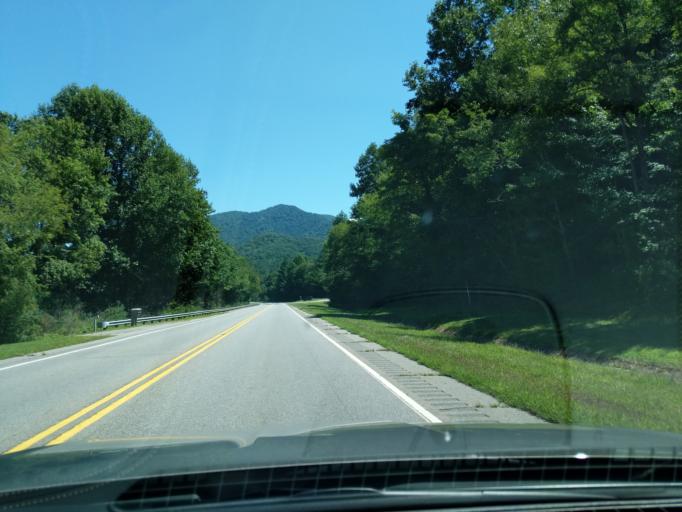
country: US
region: North Carolina
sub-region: Macon County
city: Franklin
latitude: 35.1381
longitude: -83.4964
